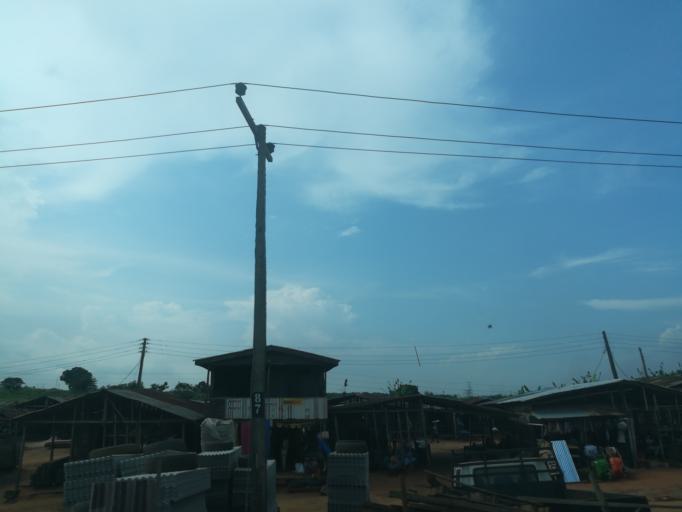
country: NG
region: Lagos
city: Ikorodu
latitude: 6.6325
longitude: 3.5331
